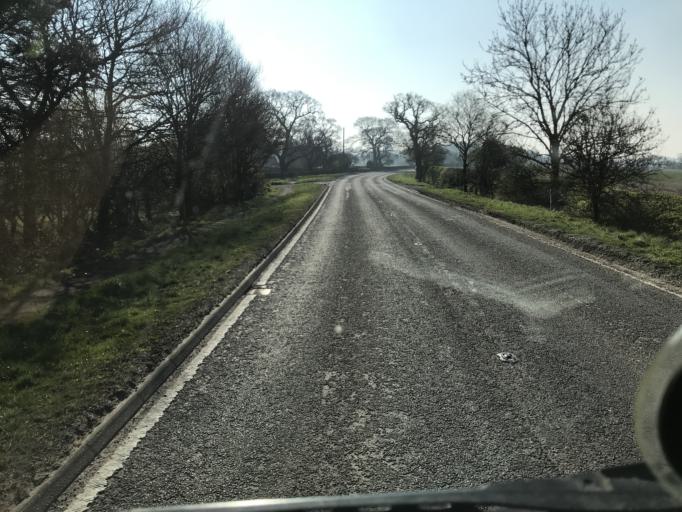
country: GB
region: England
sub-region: Cheshire West and Chester
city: Waverton
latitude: 53.1613
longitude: -2.8157
